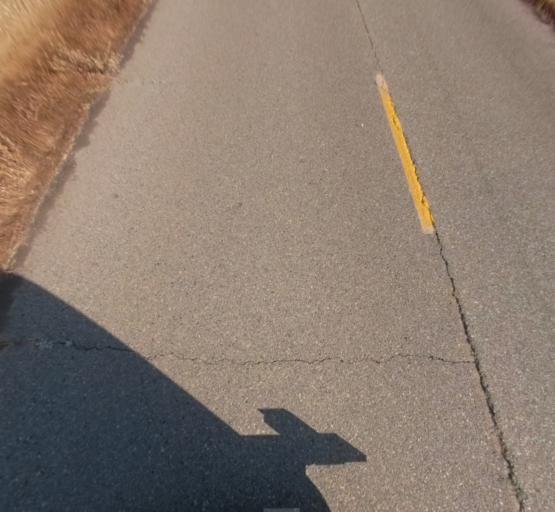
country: US
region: California
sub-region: Madera County
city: Madera Acres
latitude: 36.9889
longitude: -120.0927
